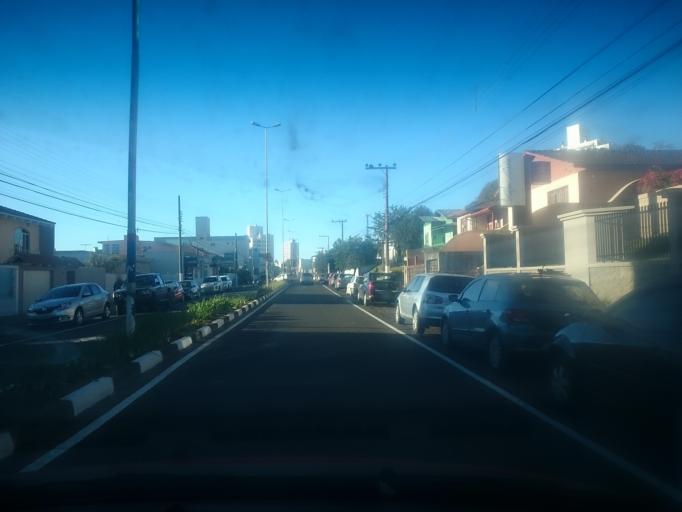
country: BR
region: Santa Catarina
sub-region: Lages
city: Lages
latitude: -27.8108
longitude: -50.3097
